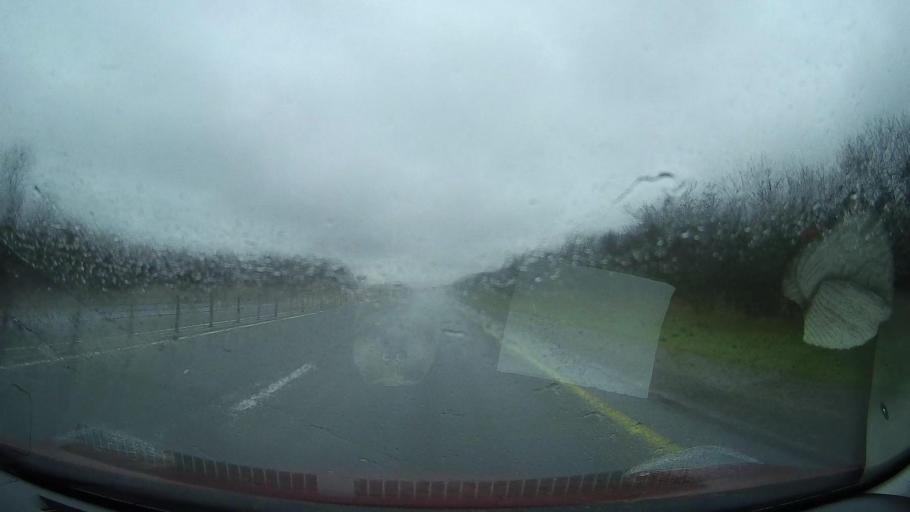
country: RU
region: Stavropol'skiy
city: Nevinnomyssk
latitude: 44.6390
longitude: 41.9787
